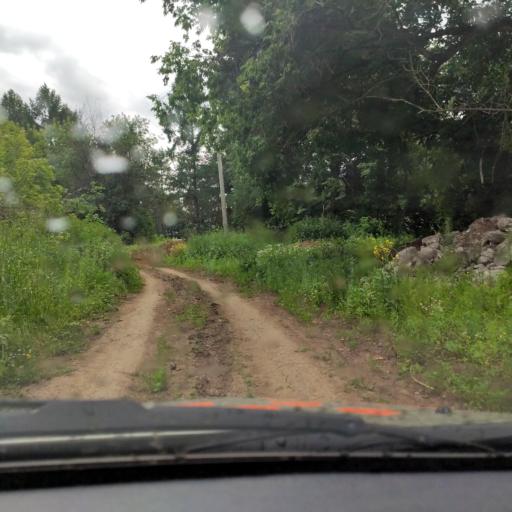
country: RU
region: Bashkortostan
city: Ufa
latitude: 54.7829
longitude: 56.1884
